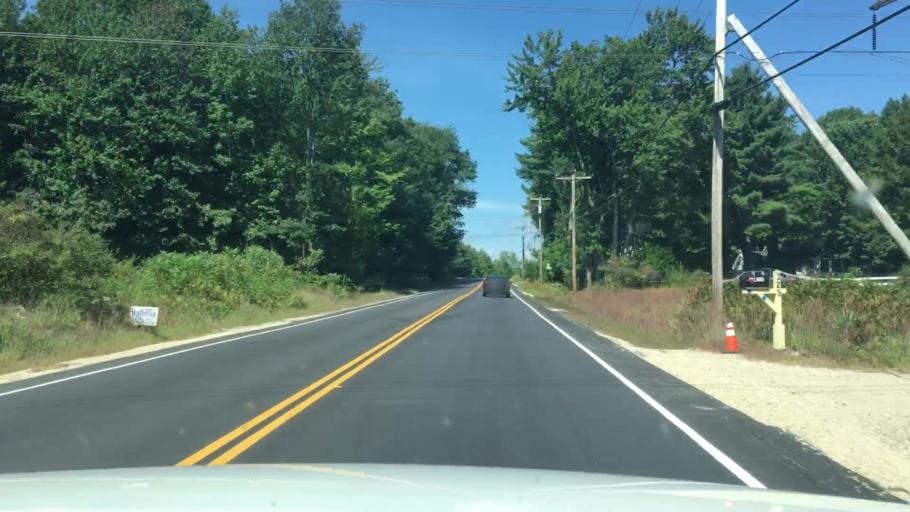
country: US
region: Maine
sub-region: Cumberland County
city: Cumberland Center
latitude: 43.8395
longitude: -70.3215
